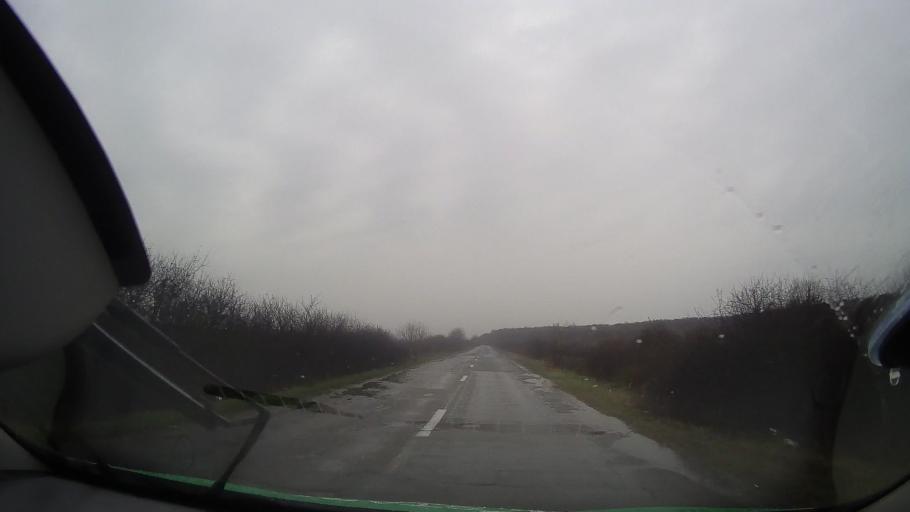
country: RO
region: Bihor
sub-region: Comuna Tinca
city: Gurbediu
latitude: 46.7900
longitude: 21.8407
